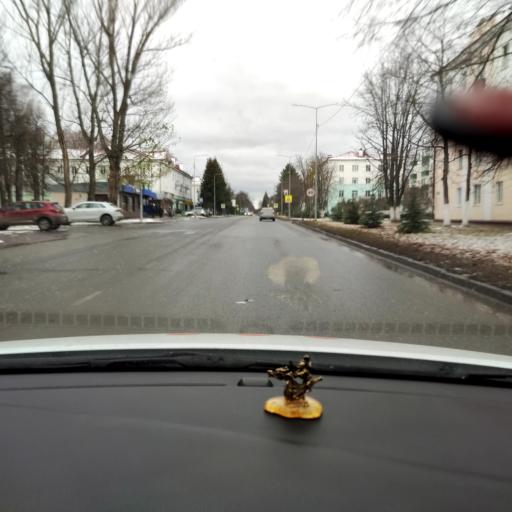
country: RU
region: Tatarstan
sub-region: Zelenodol'skiy Rayon
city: Zelenodolsk
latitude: 55.8456
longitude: 48.5194
